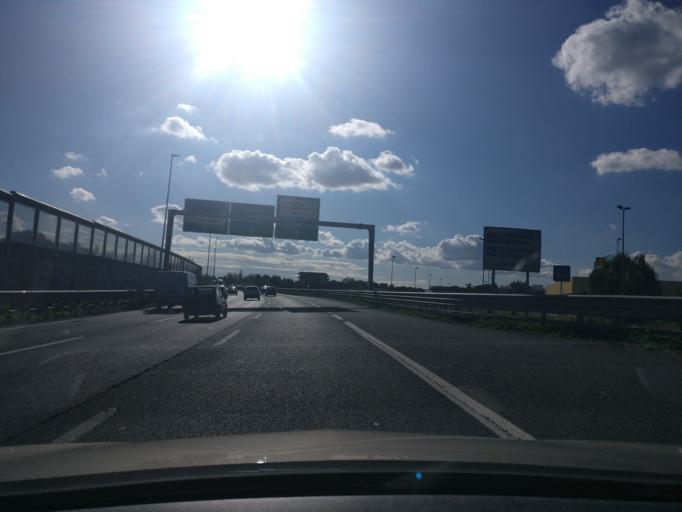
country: IT
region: Latium
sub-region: Citta metropolitana di Roma Capitale
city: Ciampino
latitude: 41.8318
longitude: 12.5841
